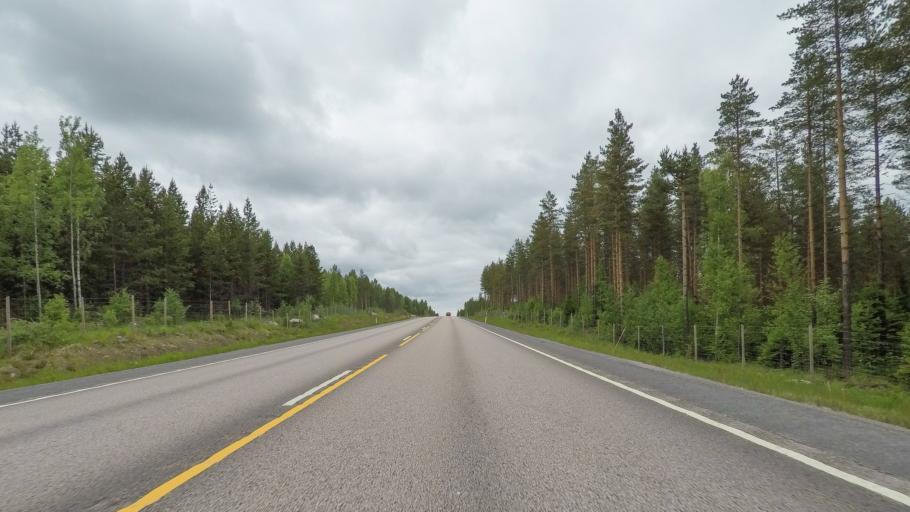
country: FI
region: Central Finland
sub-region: Jyvaeskylae
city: Toivakka
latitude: 61.9972
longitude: 26.0565
